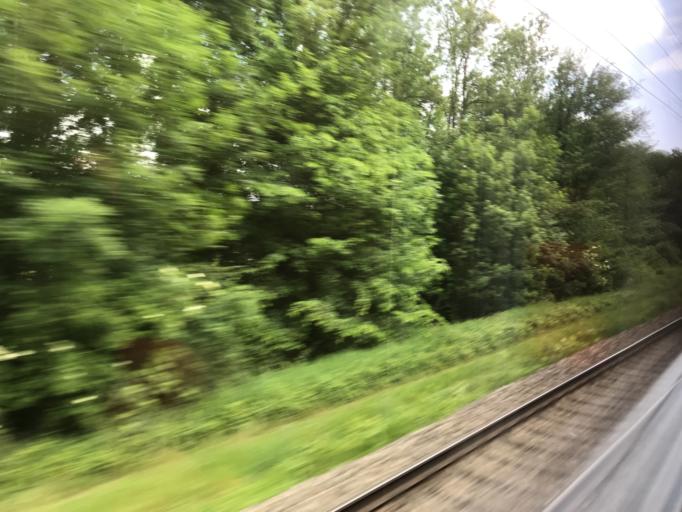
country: DE
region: Bavaria
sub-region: Swabia
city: Leipheim
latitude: 48.4579
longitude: 10.2372
